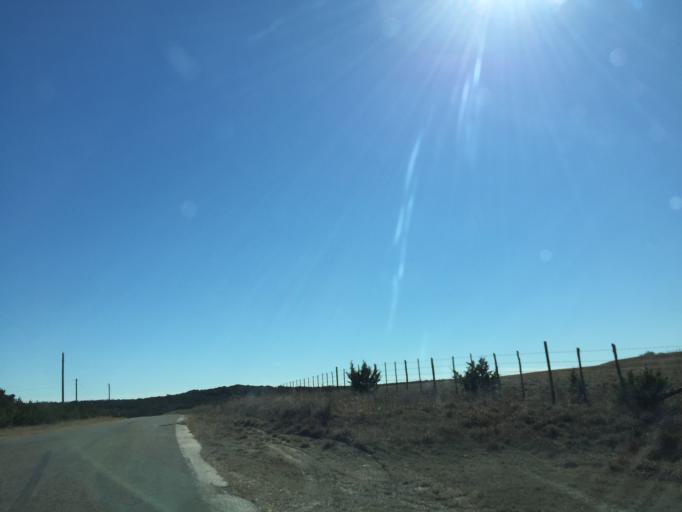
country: US
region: Texas
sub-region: Burnet County
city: Bertram
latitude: 30.8914
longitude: -98.1203
